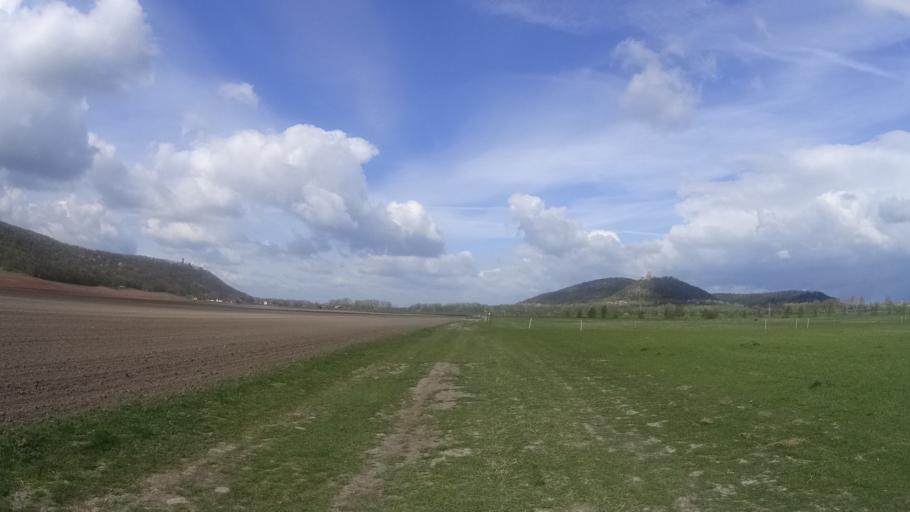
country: DE
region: Thuringia
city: Wandersleben
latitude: 50.8704
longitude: 10.8551
